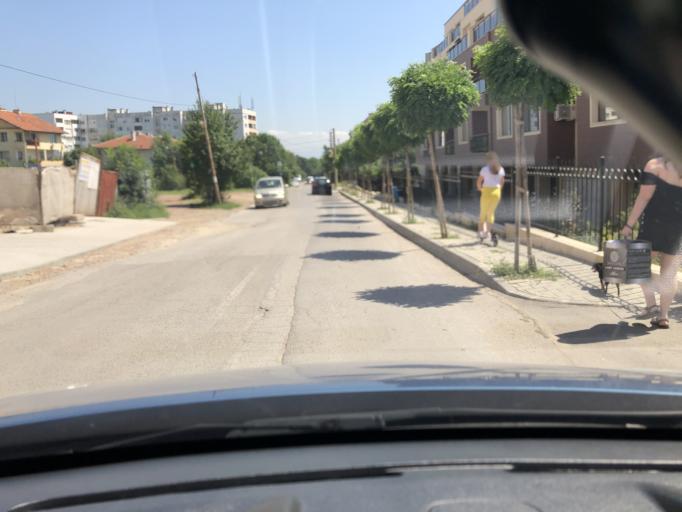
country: BG
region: Sofia-Capital
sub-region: Stolichna Obshtina
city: Sofia
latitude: 42.6784
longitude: 23.2610
